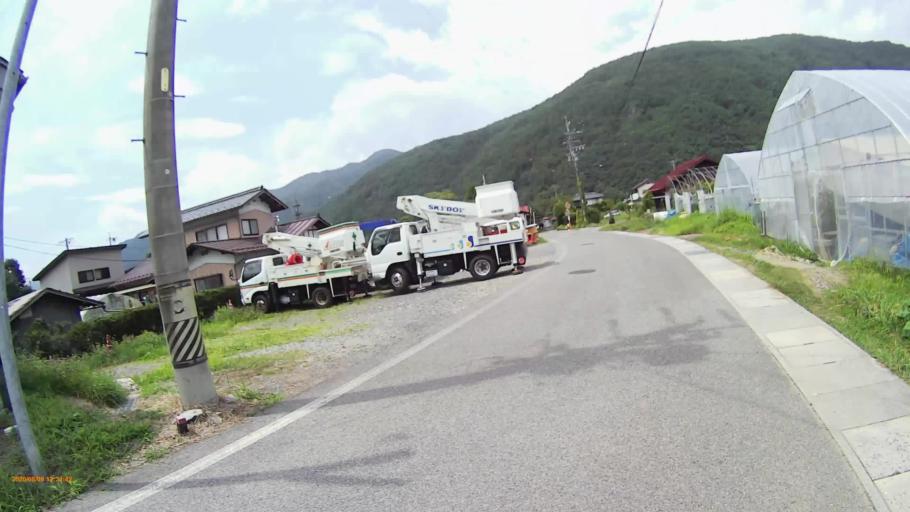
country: JP
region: Nagano
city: Ina
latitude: 35.8677
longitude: 137.7393
